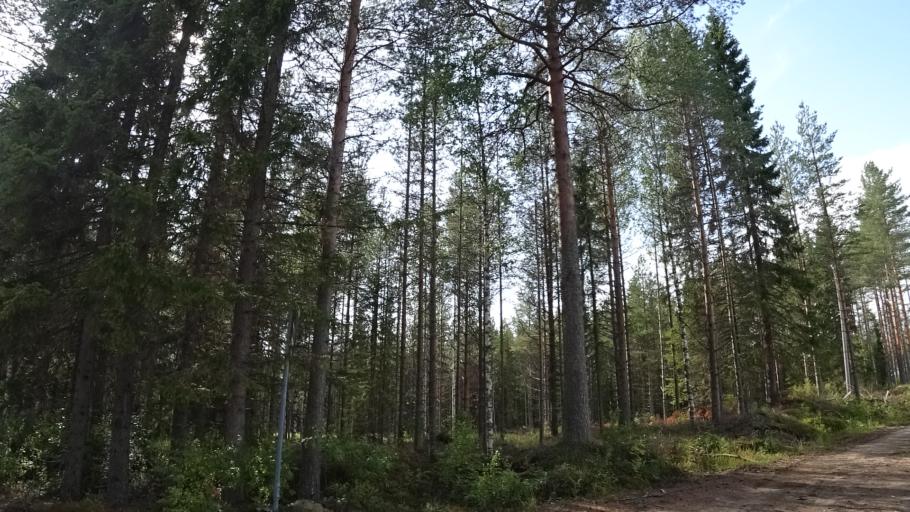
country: FI
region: North Karelia
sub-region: Pielisen Karjala
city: Lieksa
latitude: 63.5938
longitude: 30.1381
